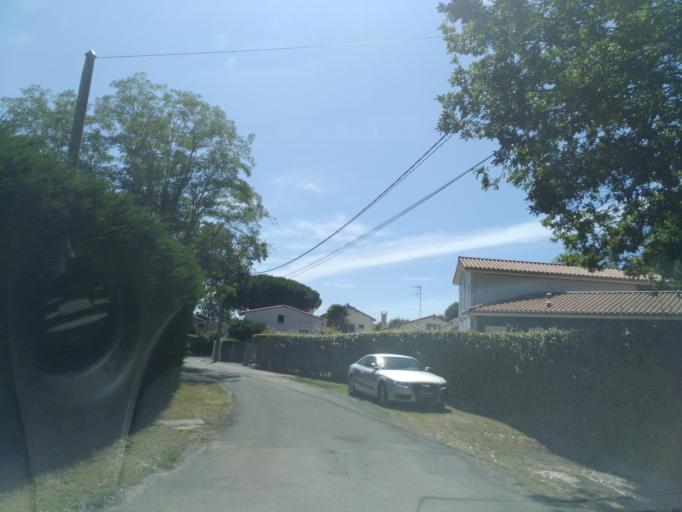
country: FR
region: Poitou-Charentes
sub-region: Departement de la Charente-Maritime
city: Saint-Palais-sur-Mer
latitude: 45.6588
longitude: -1.0782
